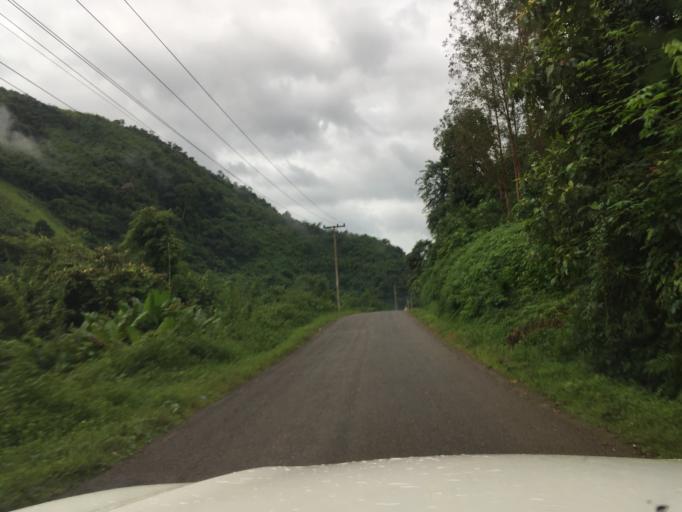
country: LA
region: Oudomxai
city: Muang La
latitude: 20.9898
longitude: 102.2277
